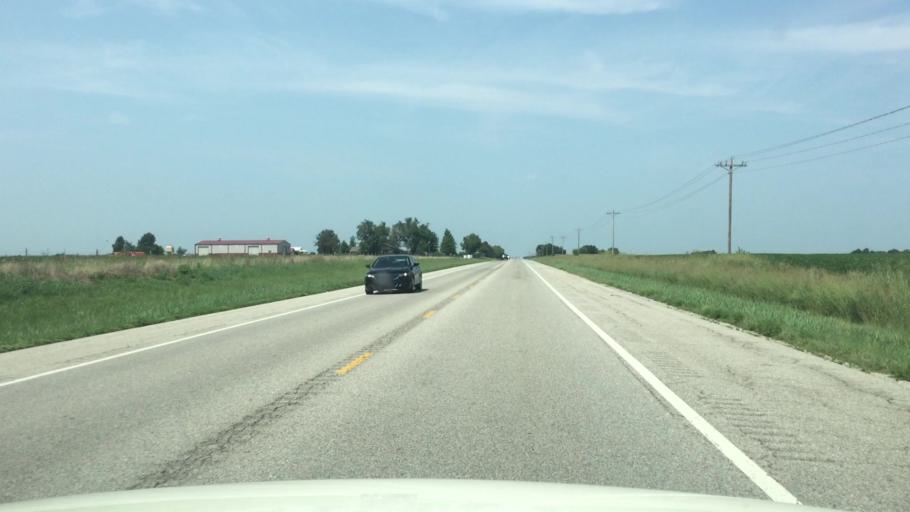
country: US
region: Kansas
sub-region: Crawford County
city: Pittsburg
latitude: 37.2687
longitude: -94.7052
